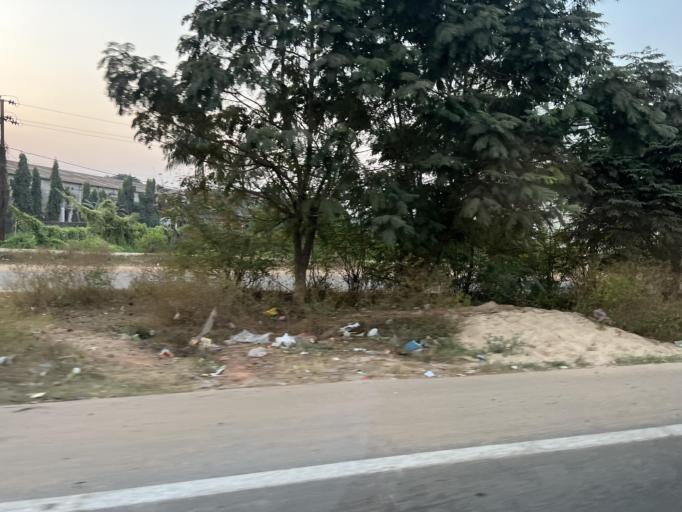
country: IN
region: Odisha
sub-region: Khordha
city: Bhubaneshwar
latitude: 20.3399
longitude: 85.8832
